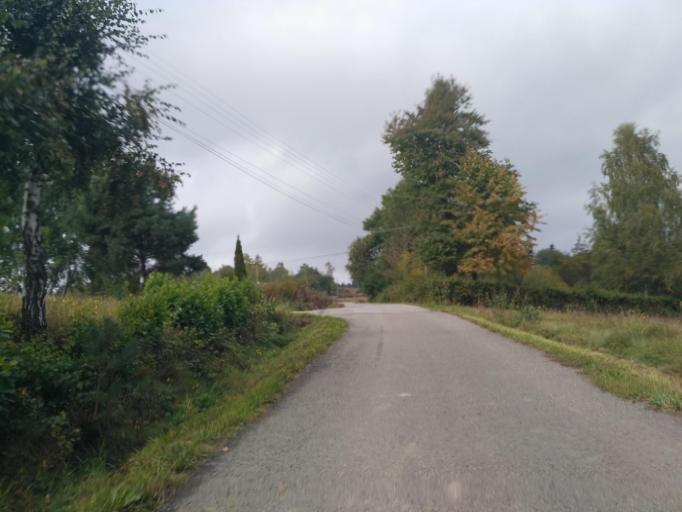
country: PL
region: Subcarpathian Voivodeship
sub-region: Powiat debicki
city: Brzostek
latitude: 49.9445
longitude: 21.4492
